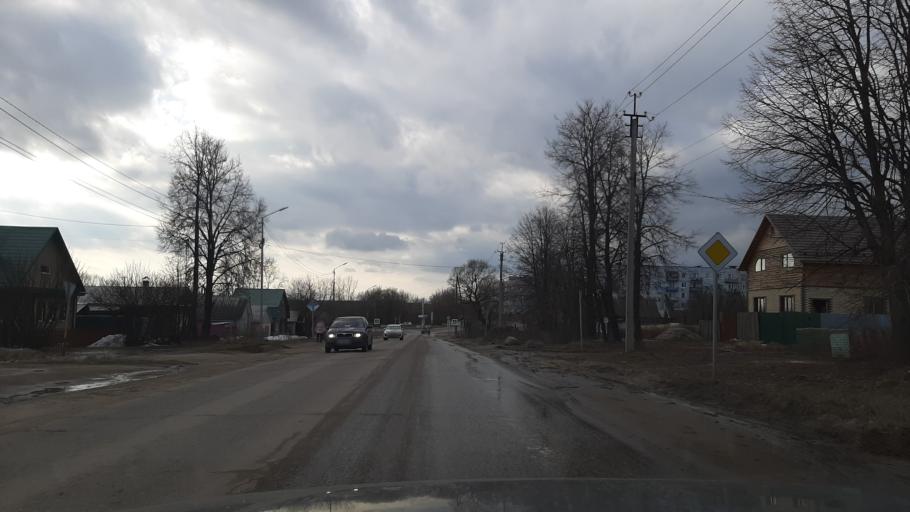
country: RU
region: Ivanovo
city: Teykovo
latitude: 56.8594
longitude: 40.5237
